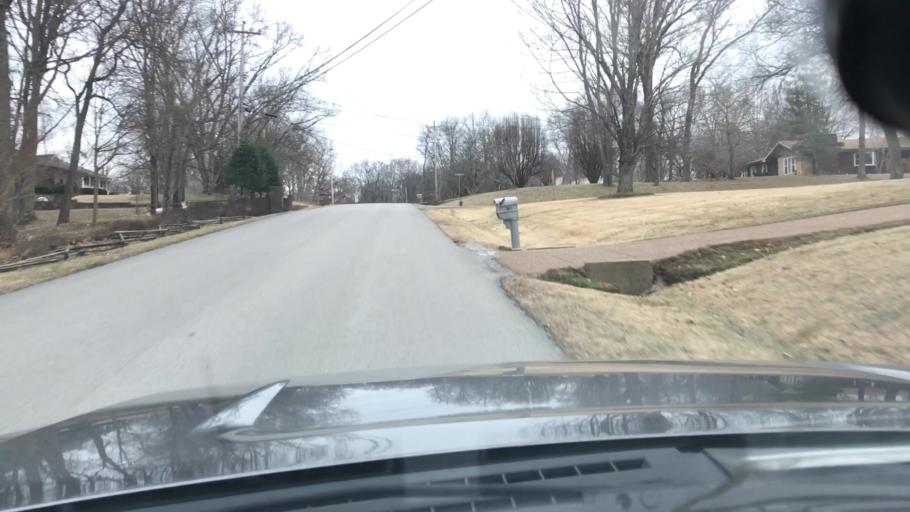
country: US
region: Tennessee
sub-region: Williamson County
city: Brentwood Estates
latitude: 36.0061
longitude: -86.7194
